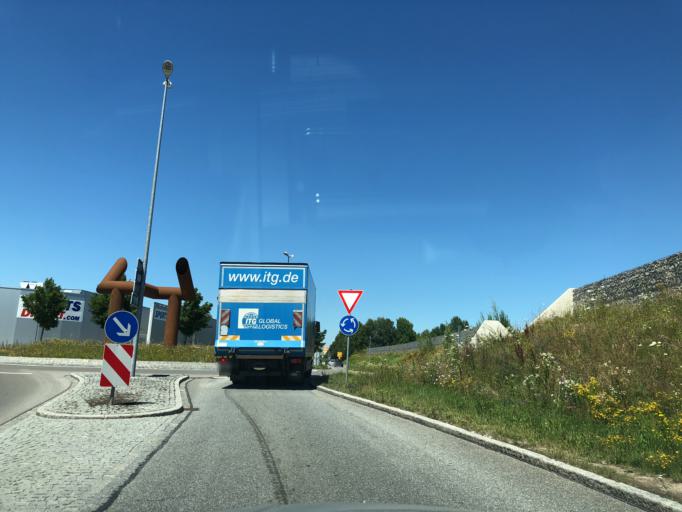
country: DE
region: Bavaria
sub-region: Upper Bavaria
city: Erding
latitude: 48.3062
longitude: 11.8922
